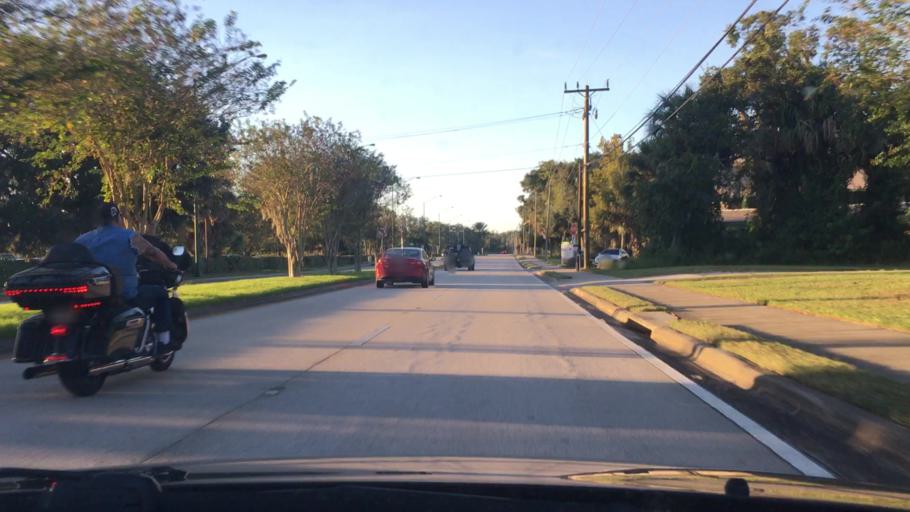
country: US
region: Florida
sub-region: Volusia County
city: Ormond Beach
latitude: 29.2878
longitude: -81.0845
